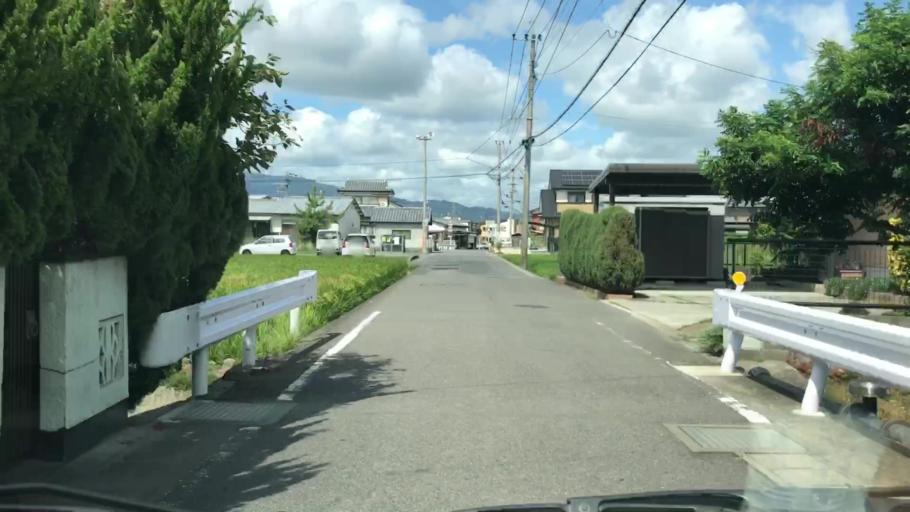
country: JP
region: Saga Prefecture
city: Saga-shi
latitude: 33.2426
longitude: 130.2019
